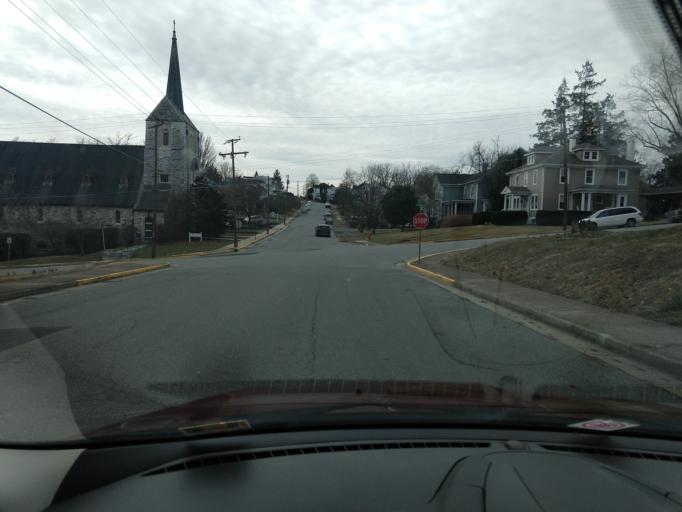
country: US
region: Virginia
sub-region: City of Waynesboro
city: Waynesboro
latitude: 38.0682
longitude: -78.8938
